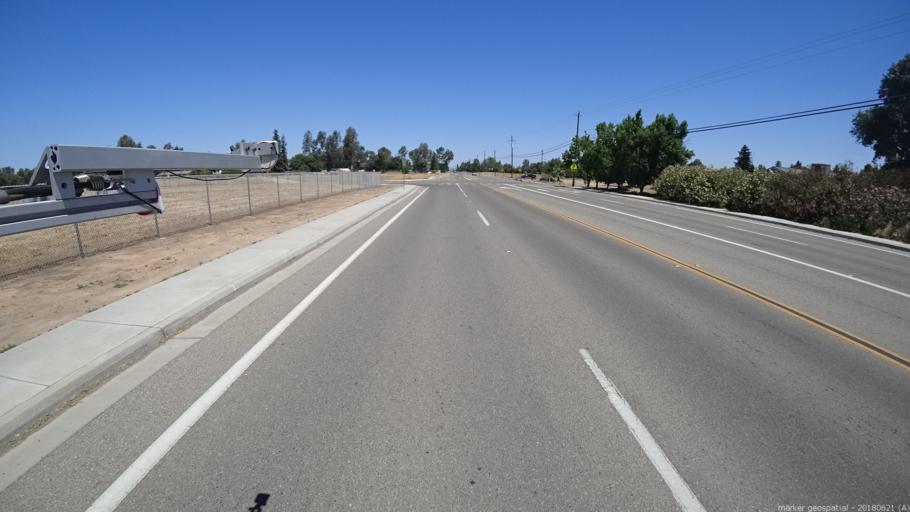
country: US
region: California
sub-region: Madera County
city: Bonadelle Ranchos-Madera Ranchos
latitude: 36.9291
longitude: -119.8943
